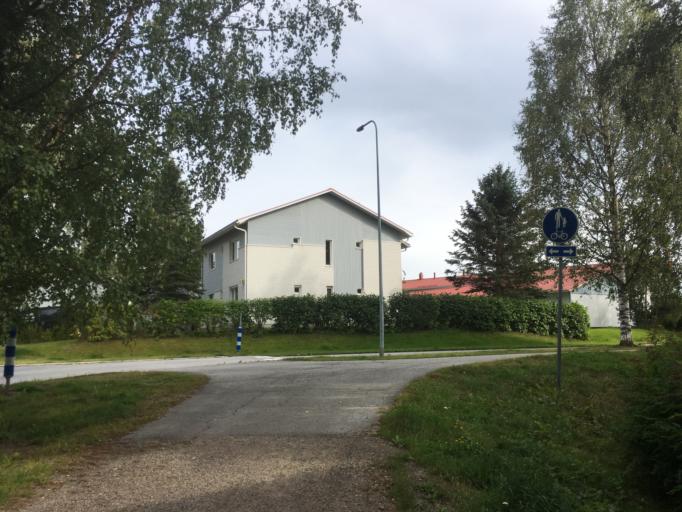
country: FI
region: Central Finland
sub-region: Jyvaeskylae
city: Jyvaeskylae
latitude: 62.2282
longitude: 25.7894
